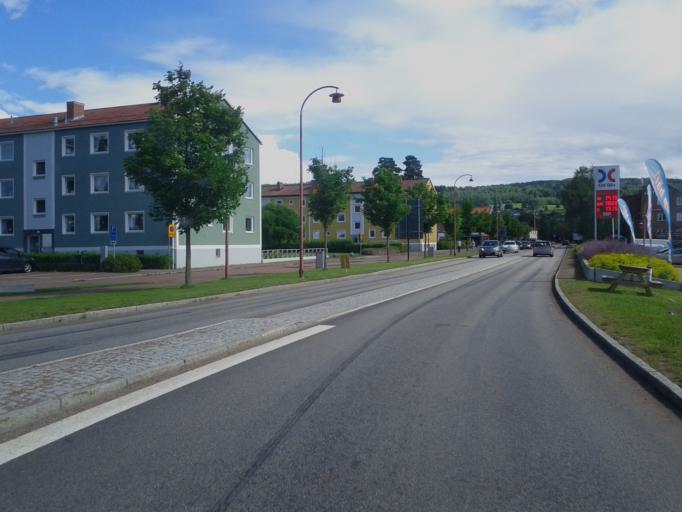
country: SE
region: Dalarna
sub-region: Rattviks Kommun
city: Raettvik
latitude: 60.8873
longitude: 15.1138
